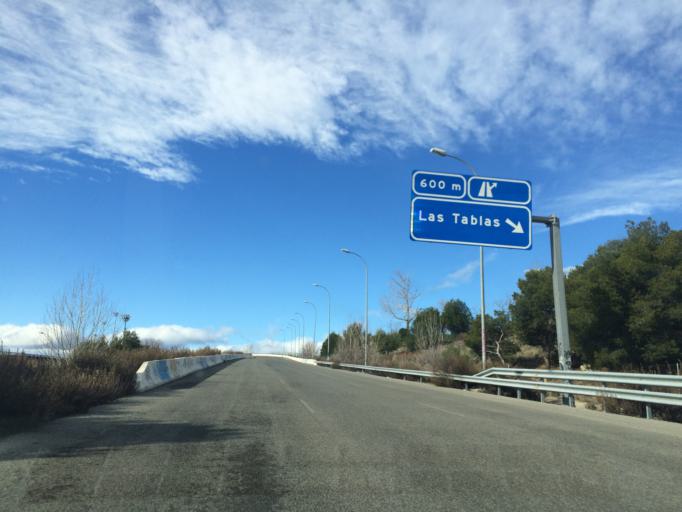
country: ES
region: Madrid
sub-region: Provincia de Madrid
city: Las Tablas
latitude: 40.5095
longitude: -3.6531
